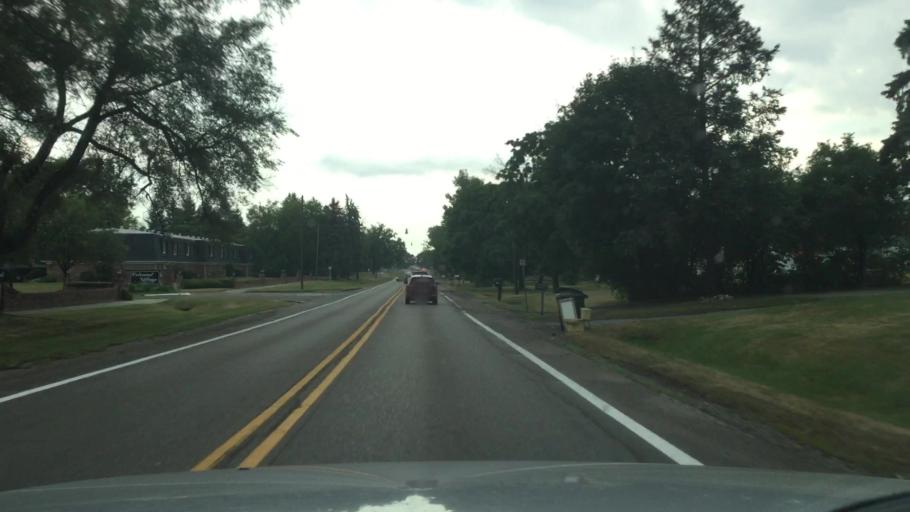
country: US
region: Michigan
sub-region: Oakland County
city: Sylvan Lake
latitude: 42.6671
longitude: -83.3471
